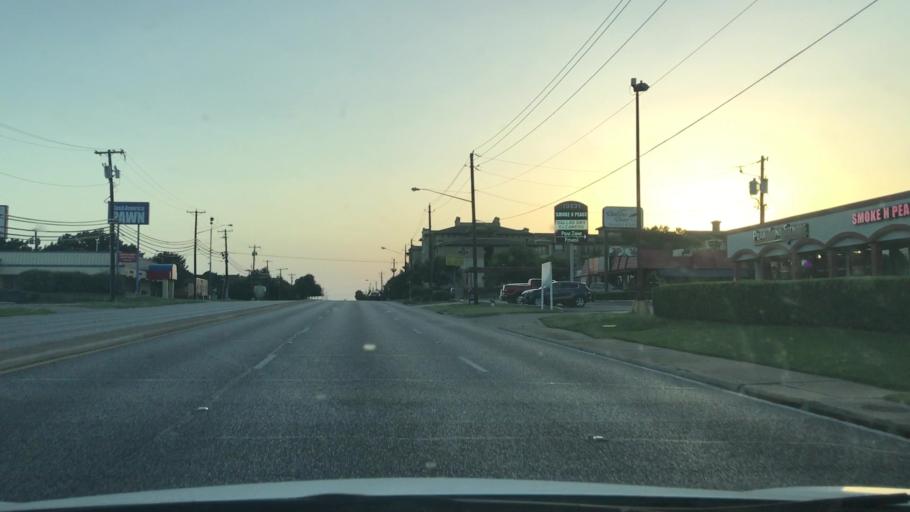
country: US
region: Texas
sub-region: Dallas County
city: Garland
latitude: 32.8643
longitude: -96.7023
